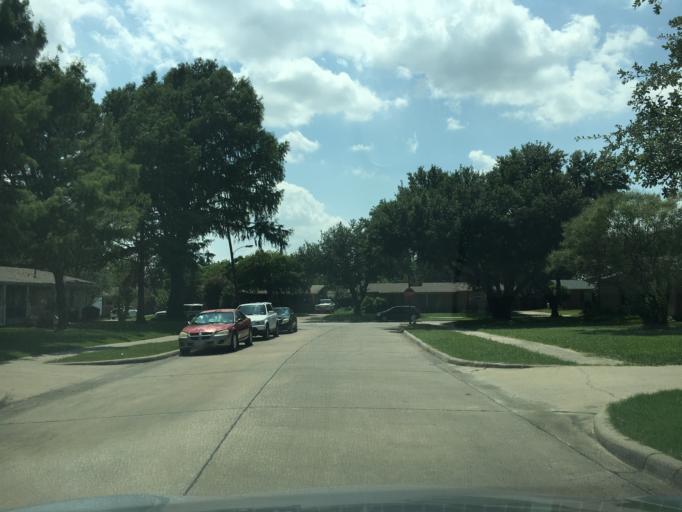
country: US
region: Texas
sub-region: Dallas County
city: Farmers Branch
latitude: 32.9177
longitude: -96.8621
